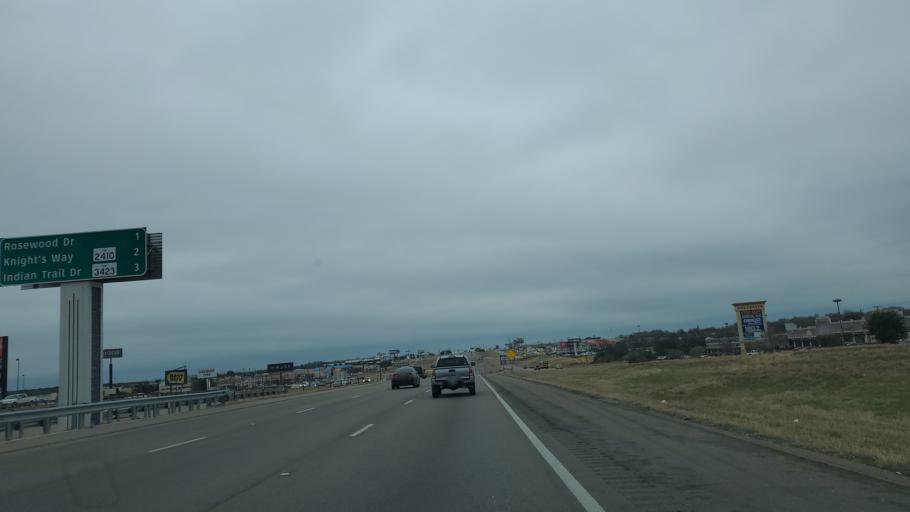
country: US
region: Texas
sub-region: Bell County
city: Killeen
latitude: 31.0864
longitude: -97.7110
